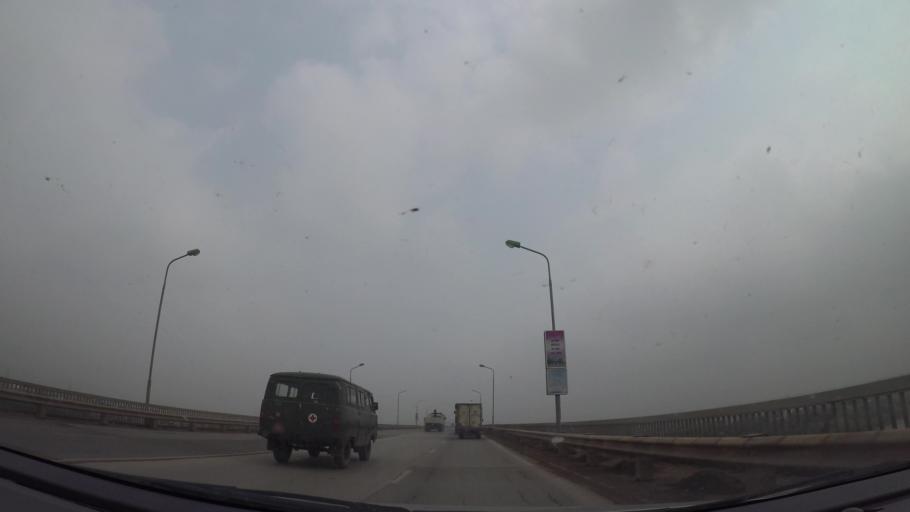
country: VN
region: Ha Noi
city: Tay Ho
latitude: 21.1000
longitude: 105.7866
